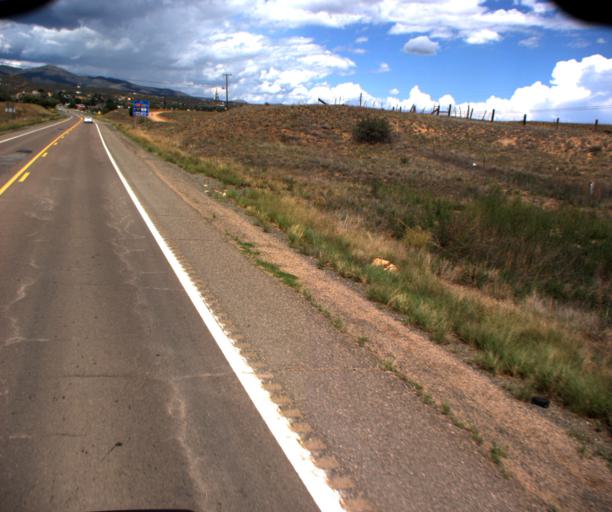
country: US
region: Arizona
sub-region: Yavapai County
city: Dewey-Humboldt
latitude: 34.5294
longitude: -112.2282
